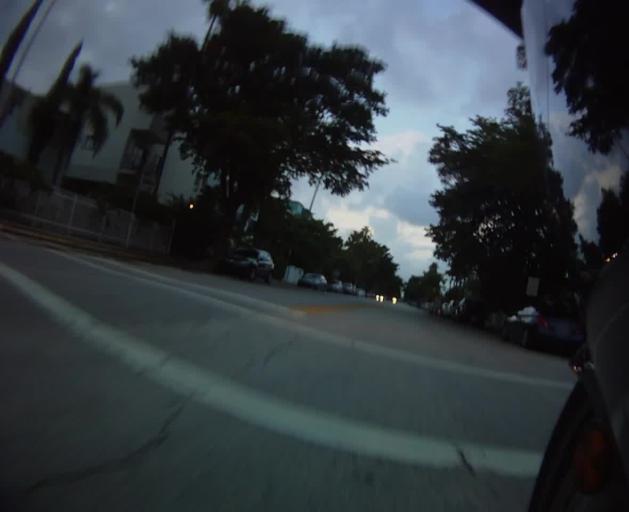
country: US
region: Florida
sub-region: Miami-Dade County
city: Miami Beach
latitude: 25.7770
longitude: -80.1384
